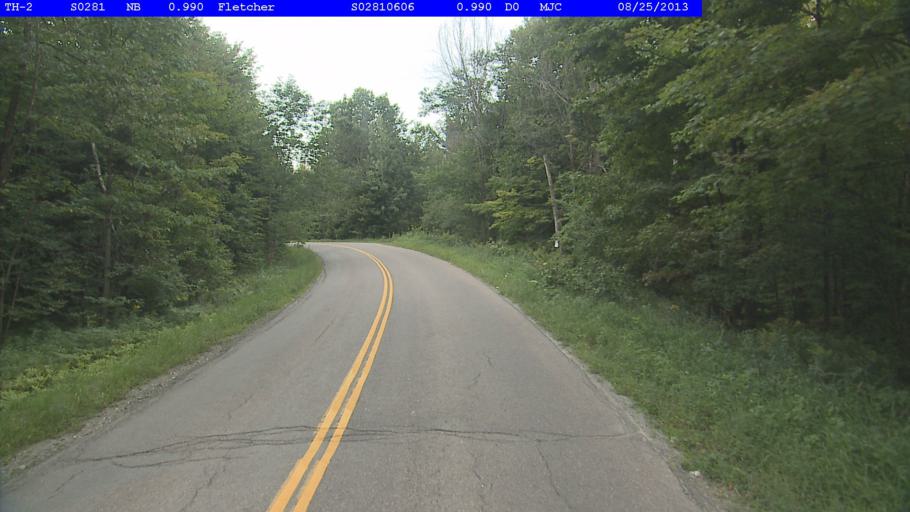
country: US
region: Vermont
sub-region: Chittenden County
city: Milton
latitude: 44.6929
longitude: -72.9275
